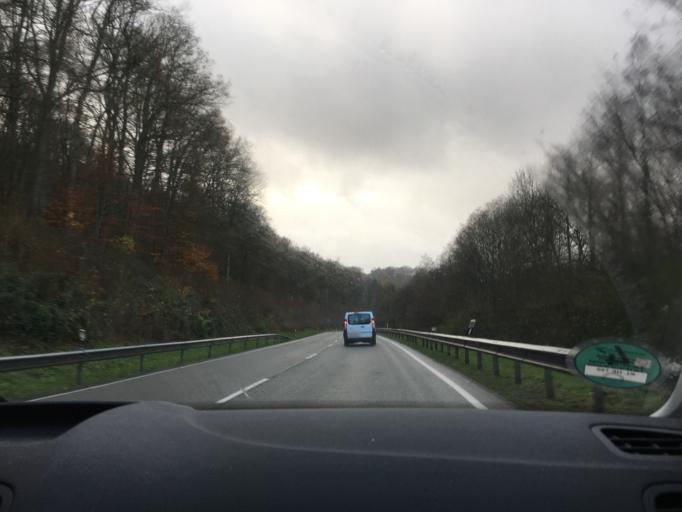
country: DE
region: Rheinland-Pfalz
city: Waldfischbach-Burgalben
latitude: 49.2849
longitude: 7.6443
